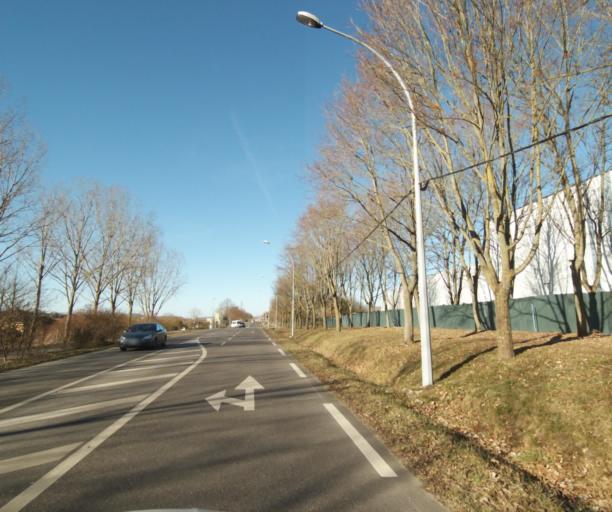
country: FR
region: Lorraine
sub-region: Departement de Meurthe-et-Moselle
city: Heillecourt
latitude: 48.6520
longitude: 6.2078
